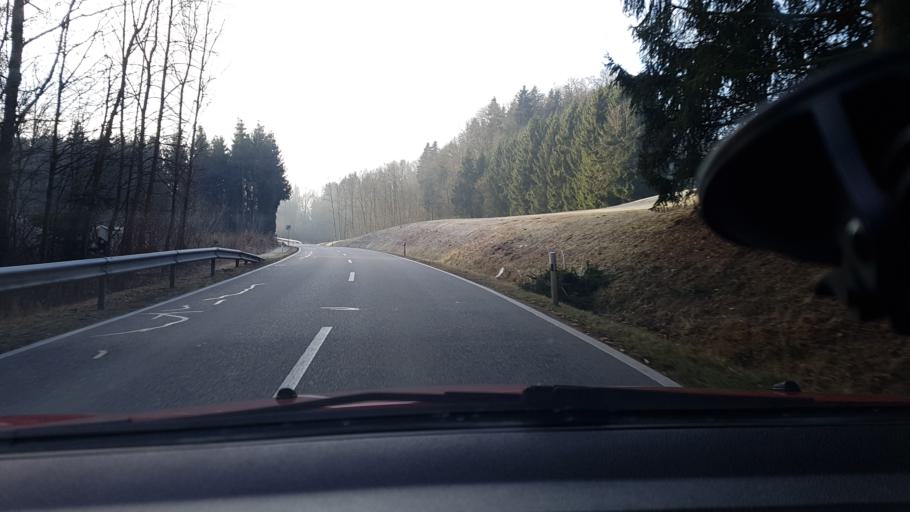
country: DE
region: Bavaria
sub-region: Lower Bavaria
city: Stubenberg
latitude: 48.2989
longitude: 13.0729
